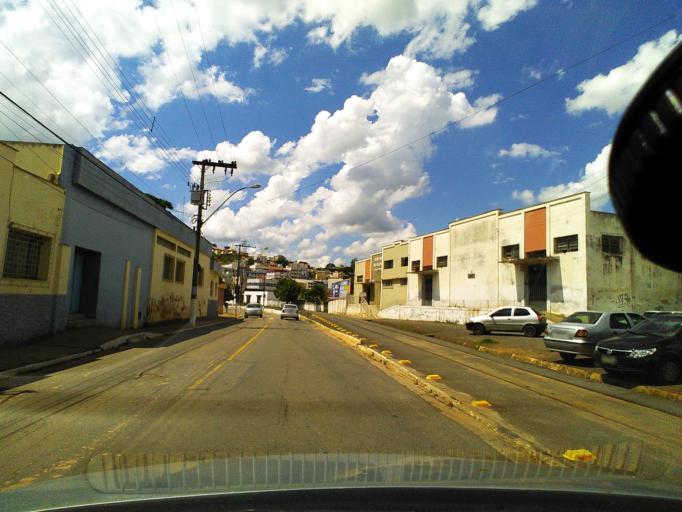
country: BR
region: Minas Gerais
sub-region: Tres Coracoes
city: Tres Coracoes
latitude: -21.6972
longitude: -45.2587
